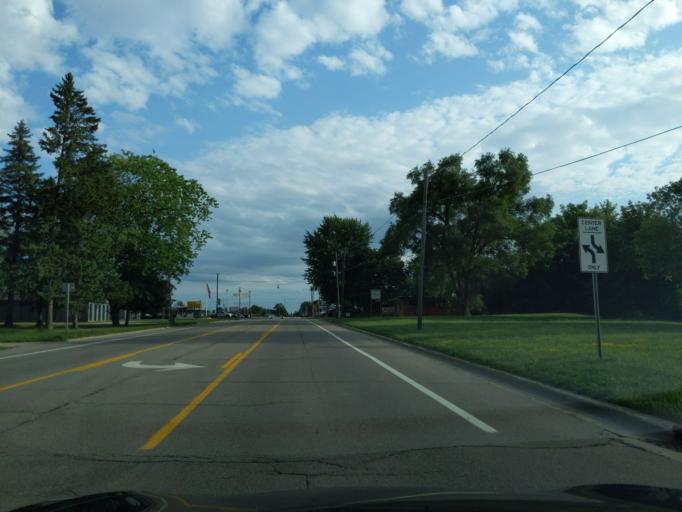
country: US
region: Michigan
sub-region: Clare County
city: Clare
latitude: 43.8138
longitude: -84.7684
